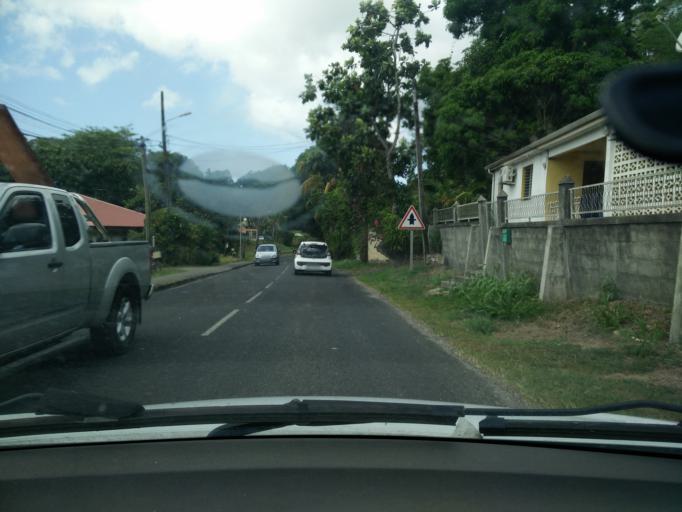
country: GP
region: Guadeloupe
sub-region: Guadeloupe
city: Les Abymes
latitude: 16.2623
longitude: -61.4966
